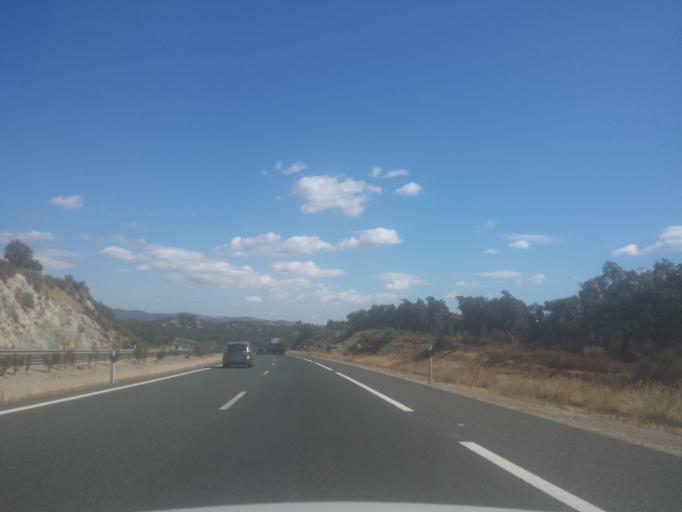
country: ES
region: Andalusia
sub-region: Provincia de Huelva
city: Santa Olalla del Cala
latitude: 37.9349
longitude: -6.2267
